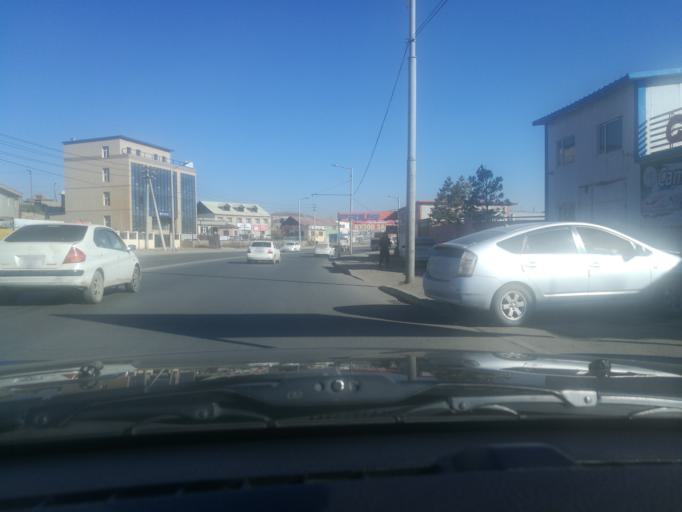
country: MN
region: Ulaanbaatar
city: Ulaanbaatar
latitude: 47.9382
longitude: 106.9098
